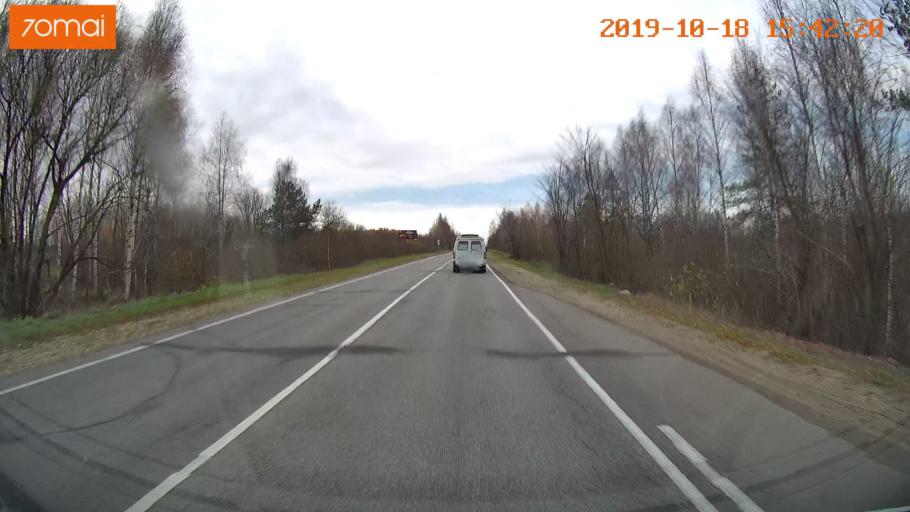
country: RU
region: Vladimir
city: Golovino
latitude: 55.9544
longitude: 40.5694
